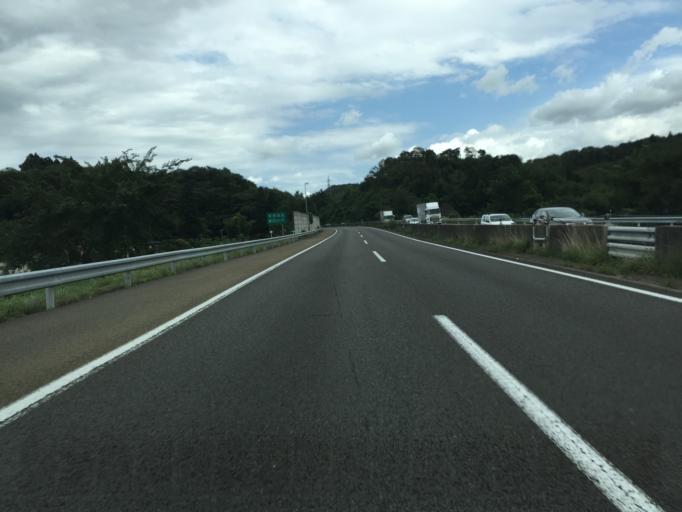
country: JP
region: Miyagi
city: Sendai
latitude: 38.1858
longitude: 140.7707
